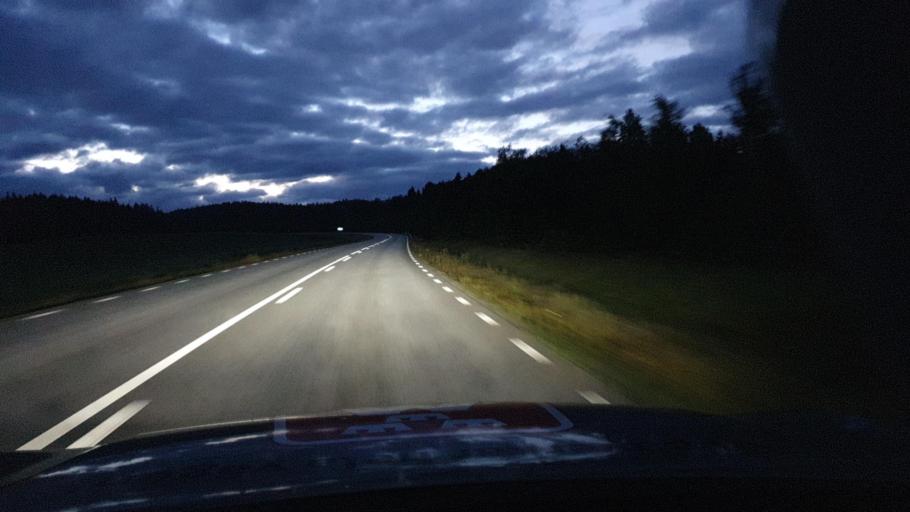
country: SE
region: OErebro
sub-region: Karlskoga Kommun
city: Karlskoga
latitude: 59.4386
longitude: 14.5126
